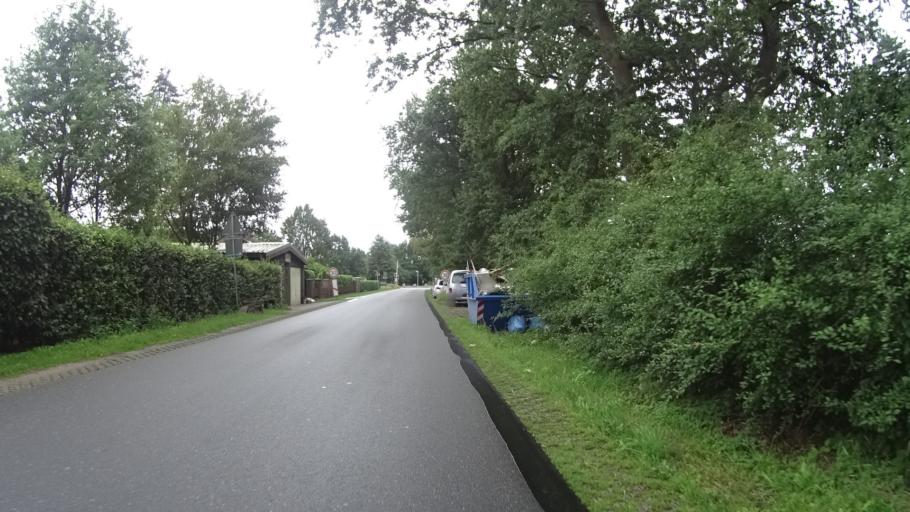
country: DE
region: Schleswig-Holstein
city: Henstedt-Ulzburg
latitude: 53.7721
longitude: 9.9709
